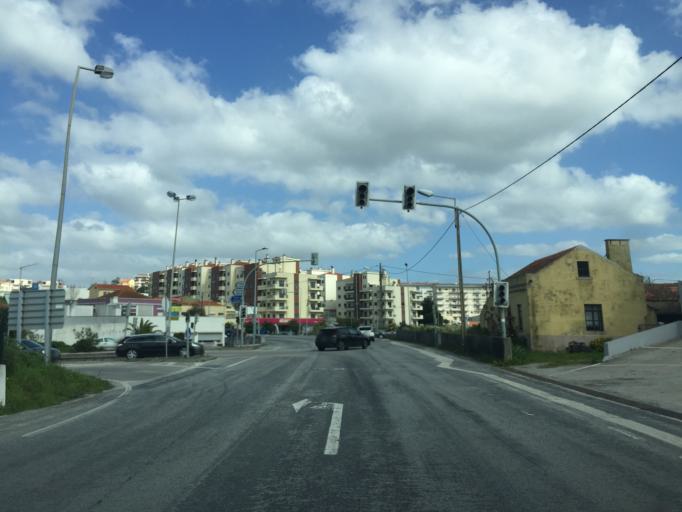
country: PT
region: Coimbra
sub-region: Figueira da Foz
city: Tavarede
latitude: 40.1641
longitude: -8.8380
